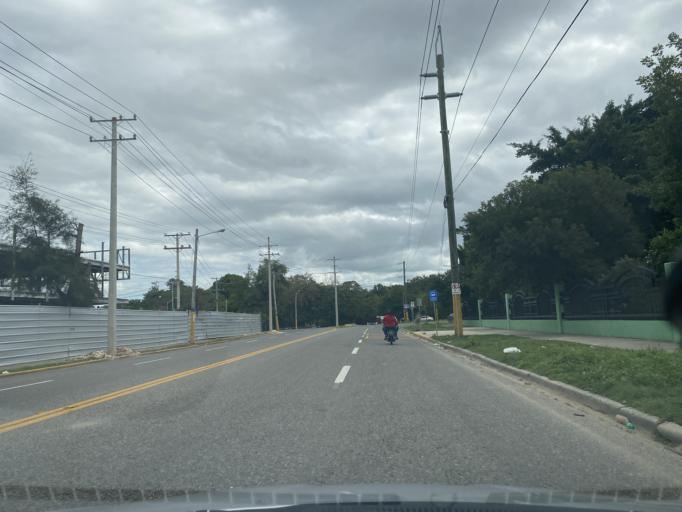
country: DO
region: Santo Domingo
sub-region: Santo Domingo
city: Santo Domingo Este
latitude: 18.4810
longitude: -69.8456
